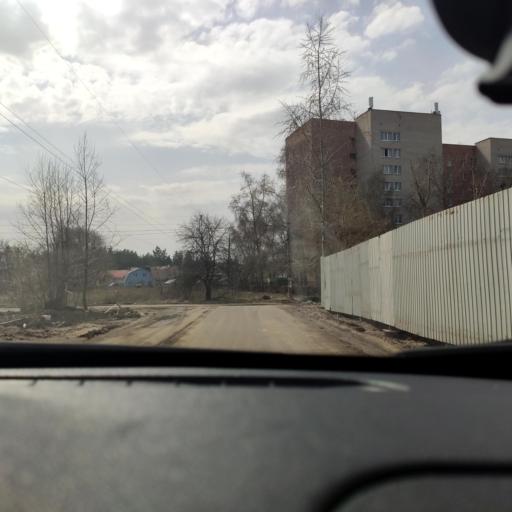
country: RU
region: Voronezj
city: Podgornoye
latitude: 51.7579
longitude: 39.1742
